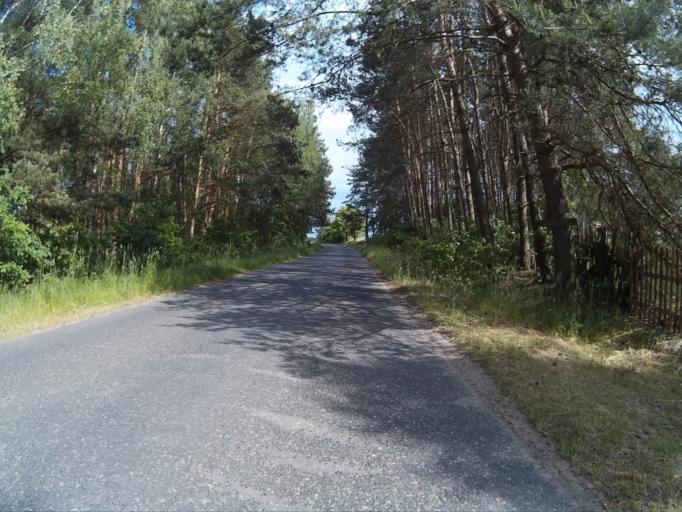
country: PL
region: Kujawsko-Pomorskie
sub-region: Powiat tucholski
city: Lubiewo
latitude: 53.4788
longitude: 17.9544
